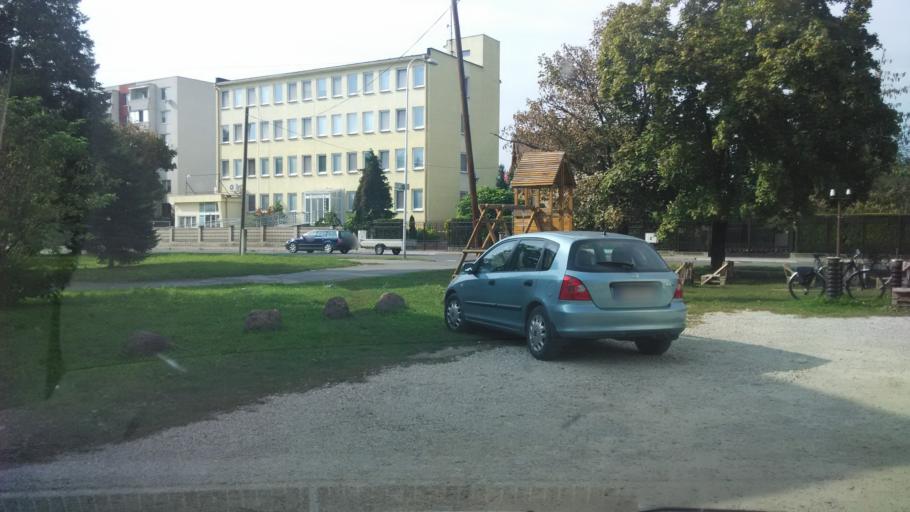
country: SK
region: Nitriansky
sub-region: Okres Nitra
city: Nitra
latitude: 48.3113
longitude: 18.0777
